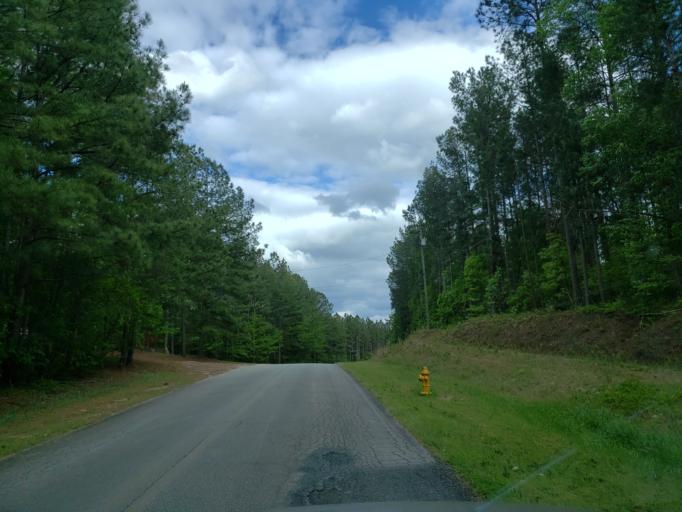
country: US
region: Georgia
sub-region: Haralson County
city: Tallapoosa
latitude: 33.8003
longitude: -85.3577
